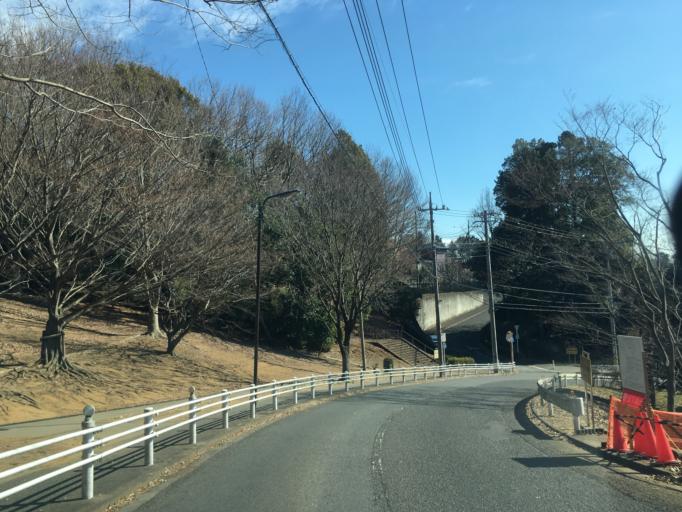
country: JP
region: Tokyo
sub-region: Machida-shi
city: Machida
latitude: 35.5834
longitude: 139.4165
